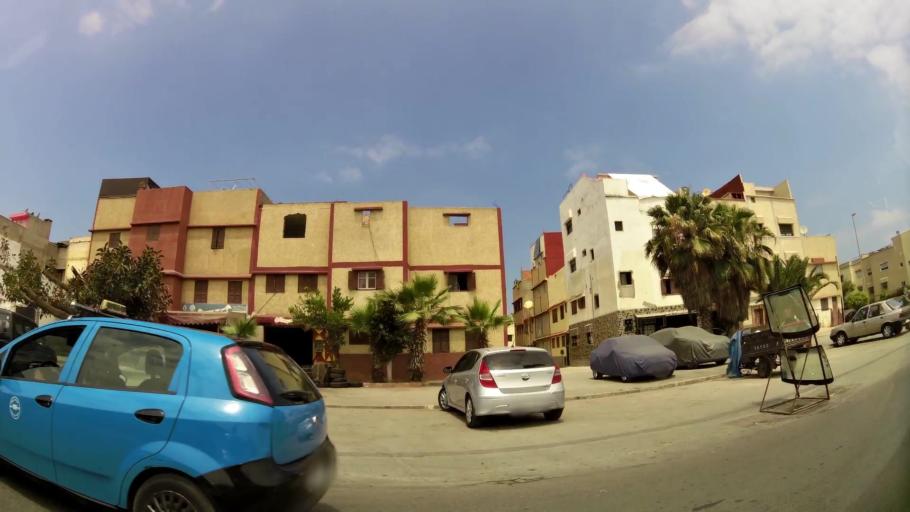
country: MA
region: Rabat-Sale-Zemmour-Zaer
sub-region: Rabat
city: Rabat
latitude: 33.9866
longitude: -6.8858
